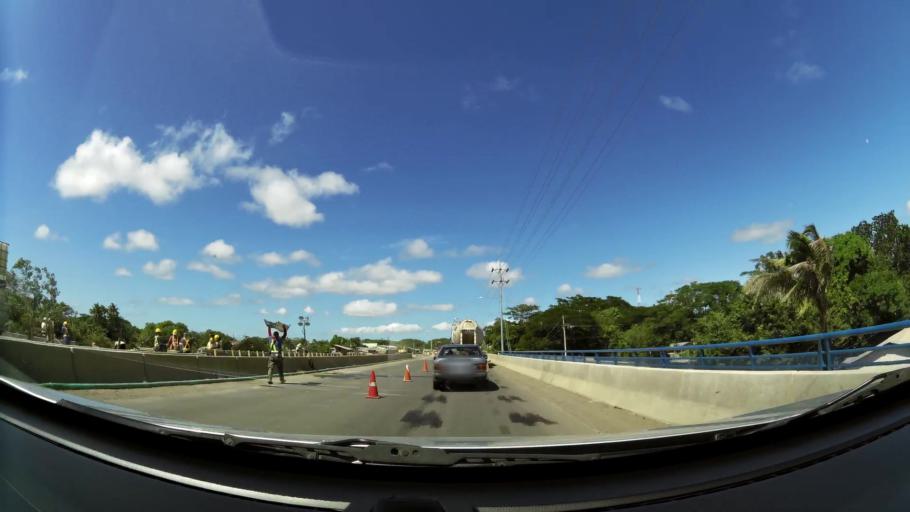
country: CR
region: Guanacaste
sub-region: Canton de Canas
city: Canas
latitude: 10.4209
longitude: -85.0886
